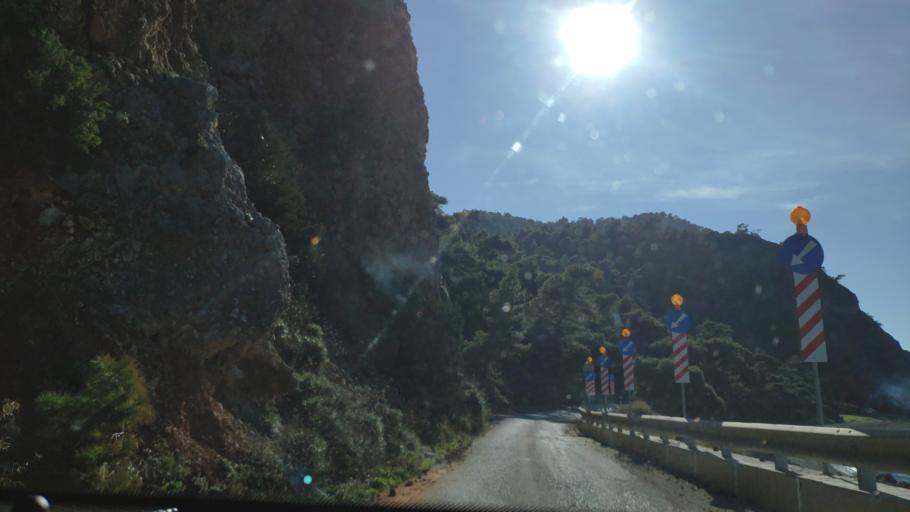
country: GR
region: Attica
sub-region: Nomarchia Dytikis Attikis
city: Kineta
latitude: 38.0655
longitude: 23.1346
